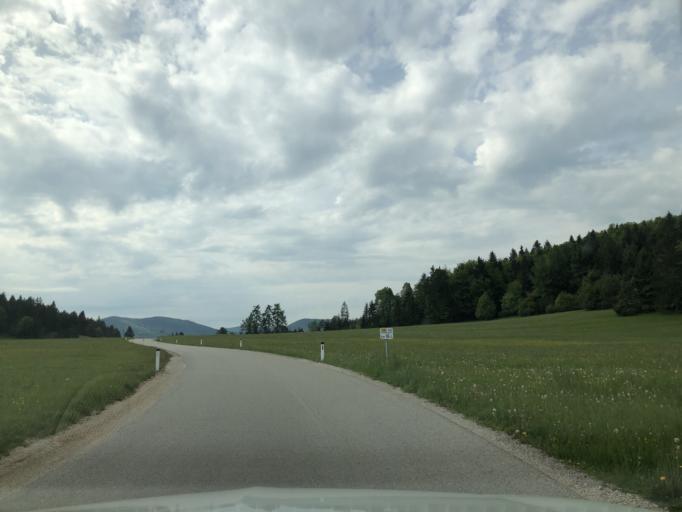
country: SI
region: Bloke
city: Nova Vas
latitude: 45.7857
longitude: 14.4991
